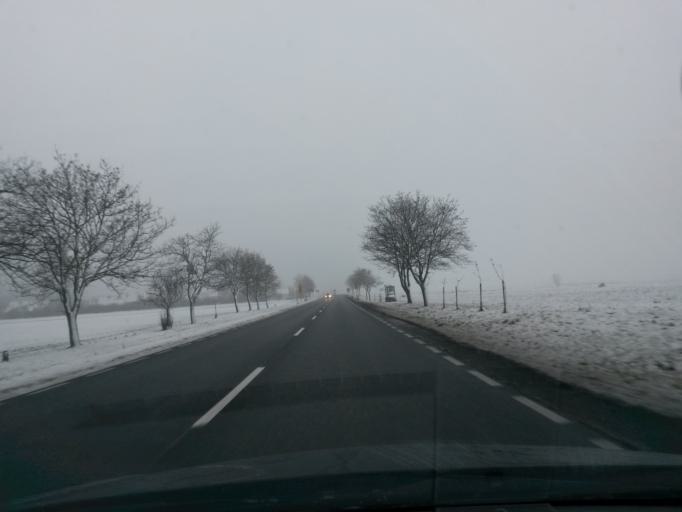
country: PL
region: Kujawsko-Pomorskie
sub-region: Powiat nakielski
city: Slesin
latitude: 53.1676
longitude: 17.7487
